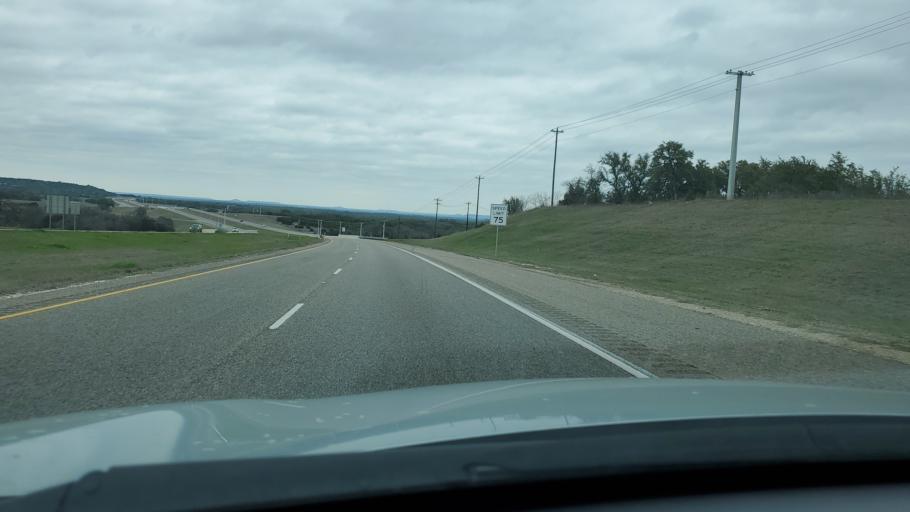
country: US
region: Texas
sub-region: Williamson County
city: Florence
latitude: 30.8666
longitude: -97.7955
